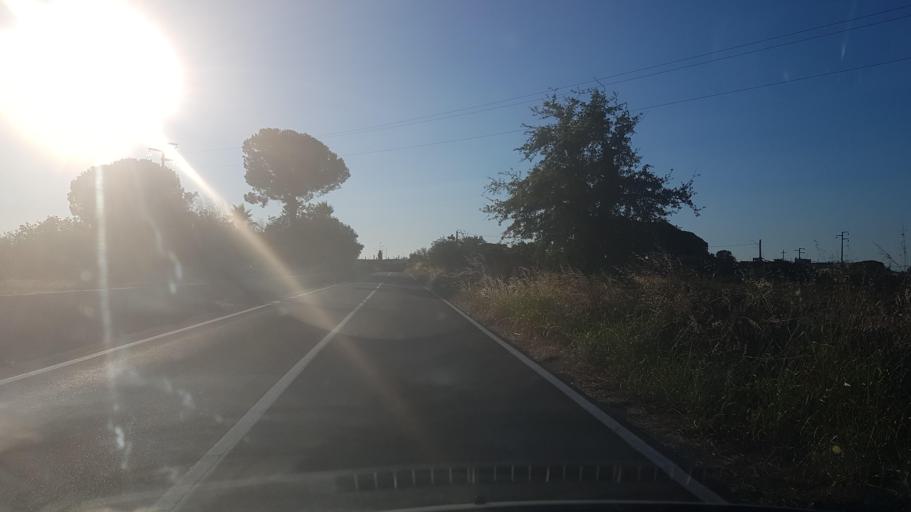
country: IT
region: Apulia
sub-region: Provincia di Lecce
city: Struda
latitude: 40.3306
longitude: 18.3001
